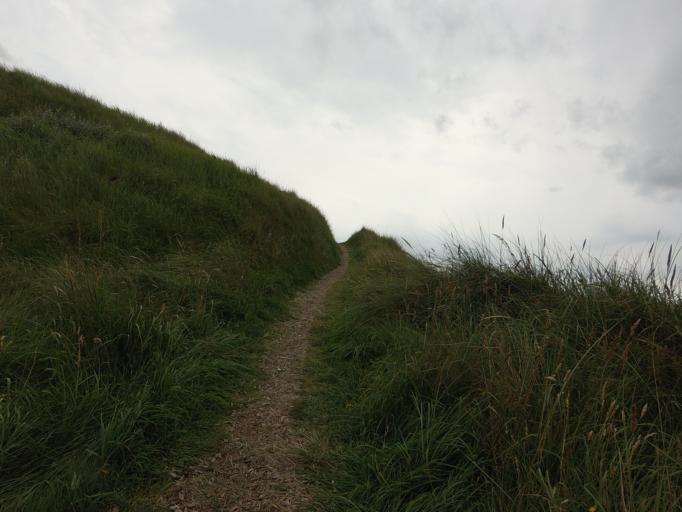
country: DK
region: North Denmark
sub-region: Jammerbugt Kommune
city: Pandrup
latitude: 57.3069
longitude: 9.6460
